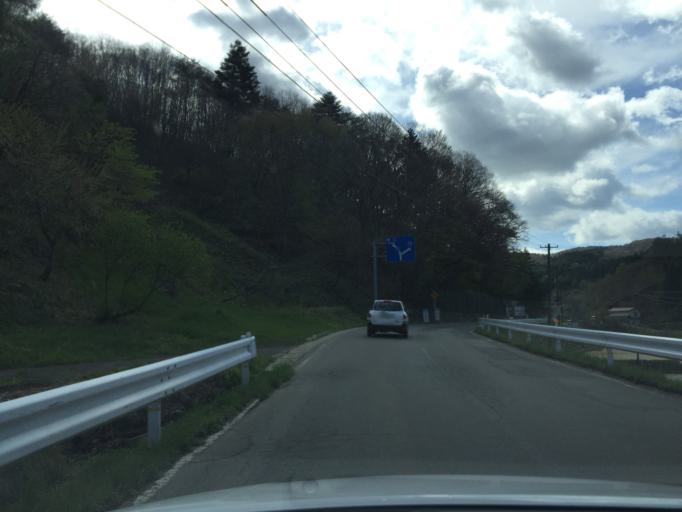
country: JP
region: Fukushima
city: Funehikimachi-funehiki
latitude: 37.5872
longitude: 140.6910
